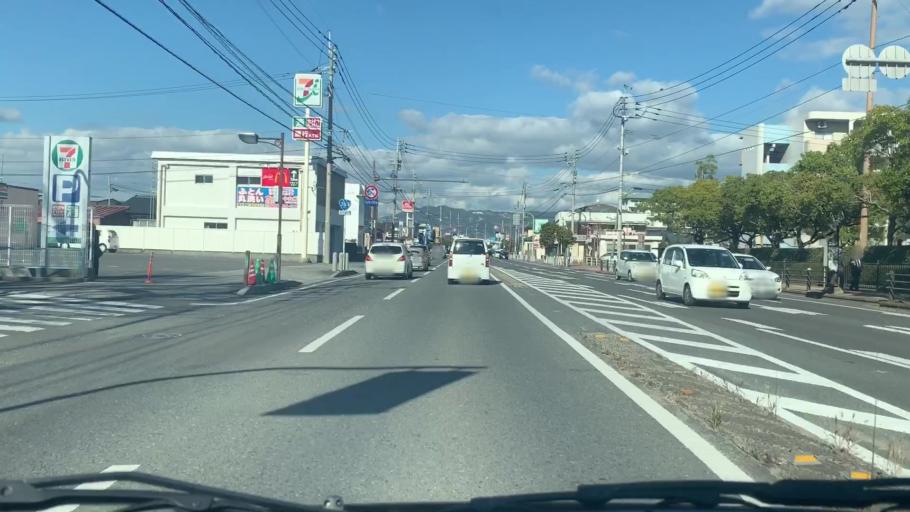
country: JP
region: Saga Prefecture
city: Saga-shi
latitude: 33.2780
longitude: 130.2928
